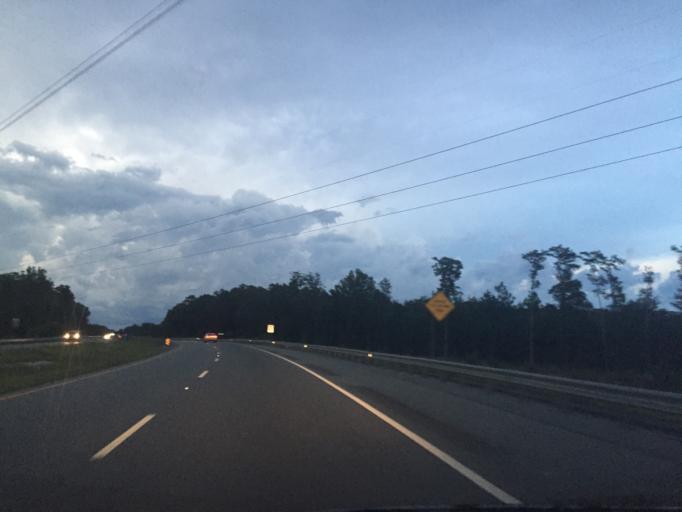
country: US
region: Georgia
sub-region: Liberty County
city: Midway
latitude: 31.8284
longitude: -81.4904
